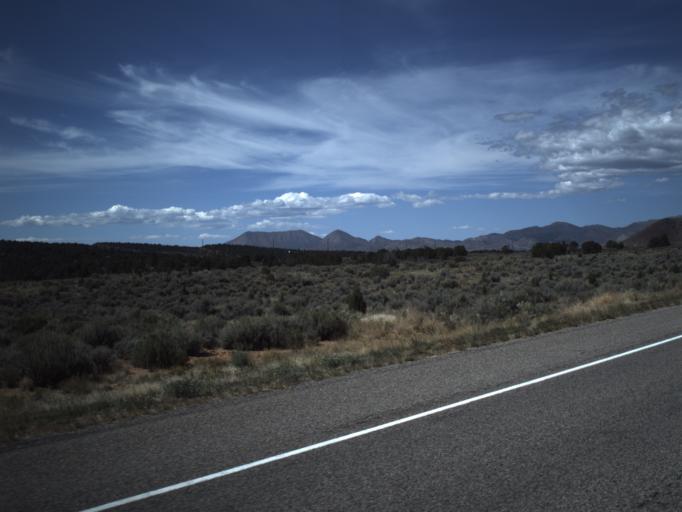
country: US
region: Utah
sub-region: Washington County
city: Ivins
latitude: 37.2842
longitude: -113.6553
